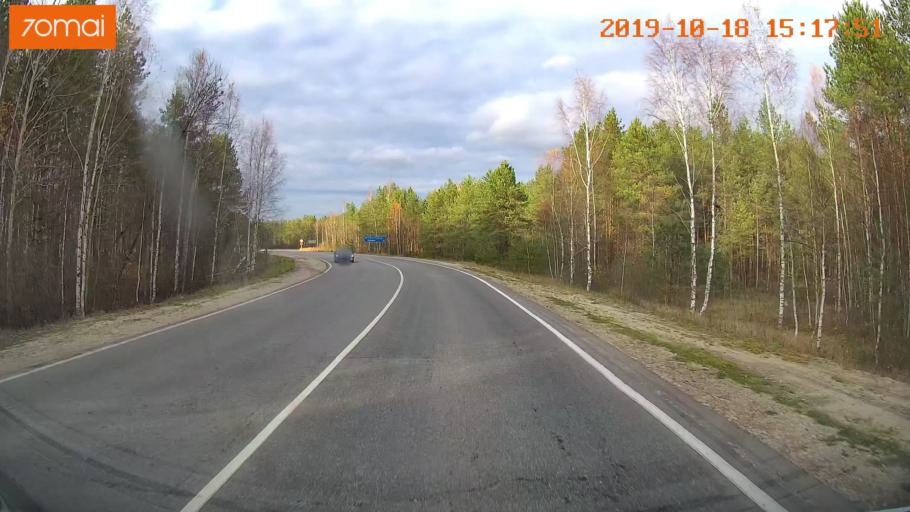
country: RU
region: Vladimir
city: Anopino
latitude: 55.6558
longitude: 40.7273
